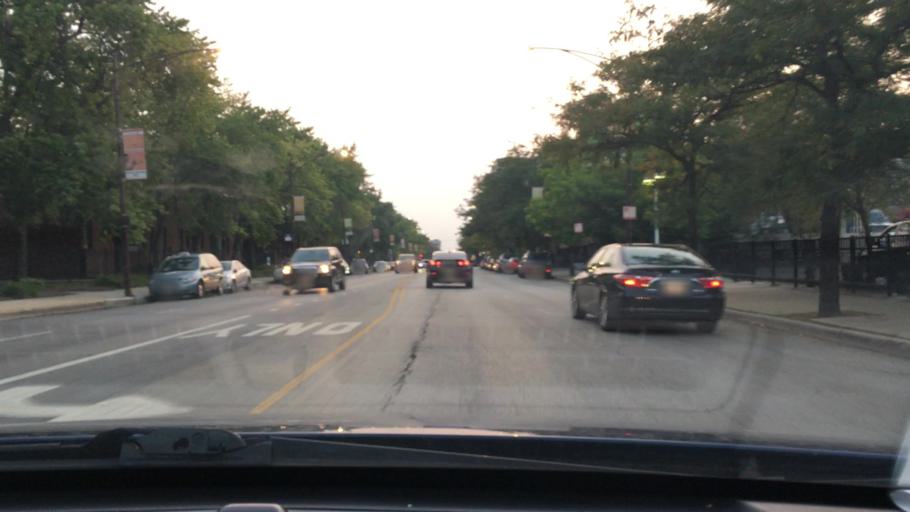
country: US
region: Illinois
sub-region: Cook County
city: Chicago
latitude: 41.8097
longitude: -87.5970
